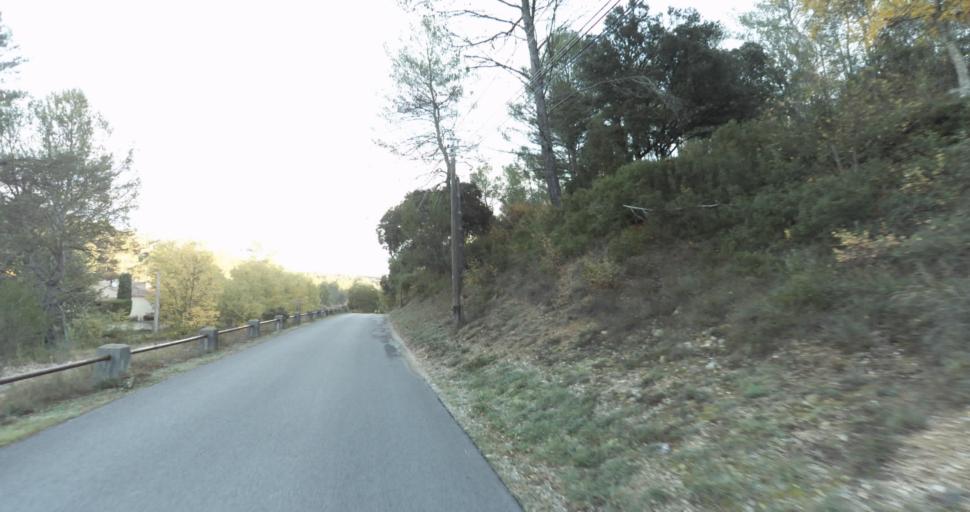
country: FR
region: Provence-Alpes-Cote d'Azur
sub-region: Departement des Bouches-du-Rhone
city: Venelles
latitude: 43.5878
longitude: 5.5078
